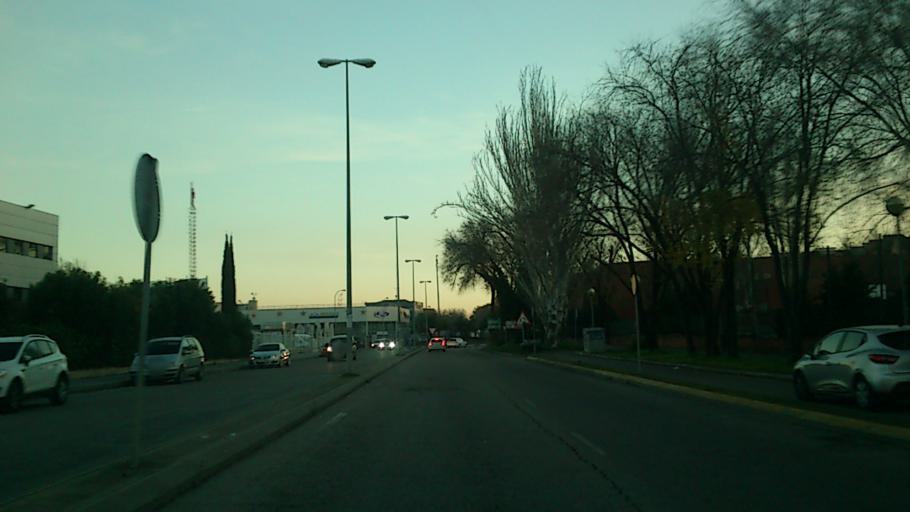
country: ES
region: Madrid
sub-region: Provincia de Madrid
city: San Fernando de Henares
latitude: 40.4339
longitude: -3.5400
